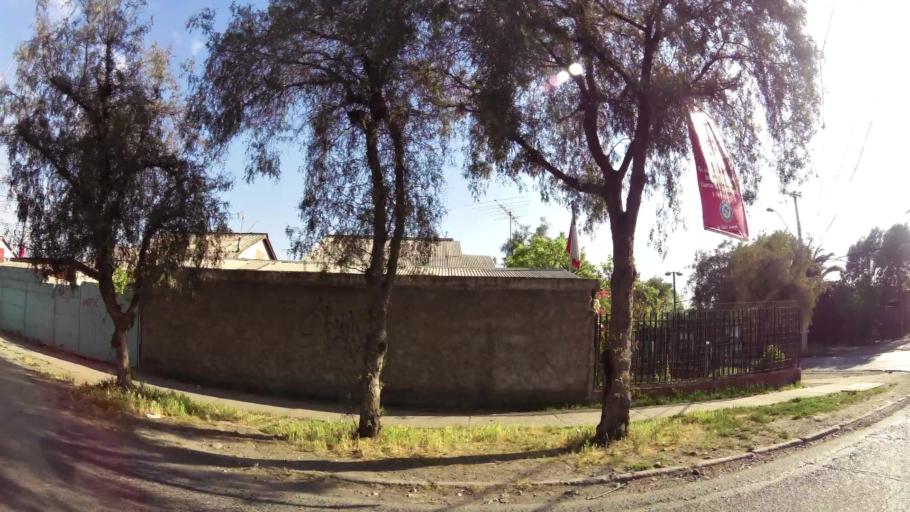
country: CL
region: Santiago Metropolitan
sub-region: Provincia de Santiago
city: La Pintana
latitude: -33.5651
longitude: -70.5967
